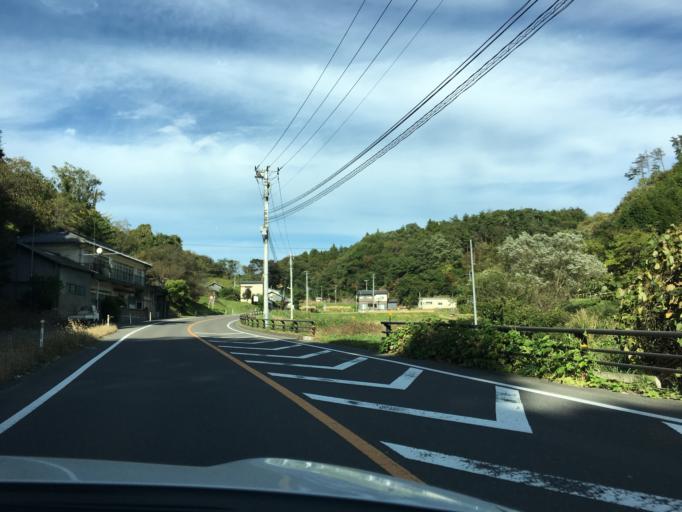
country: JP
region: Fukushima
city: Miharu
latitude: 37.3595
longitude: 140.4930
